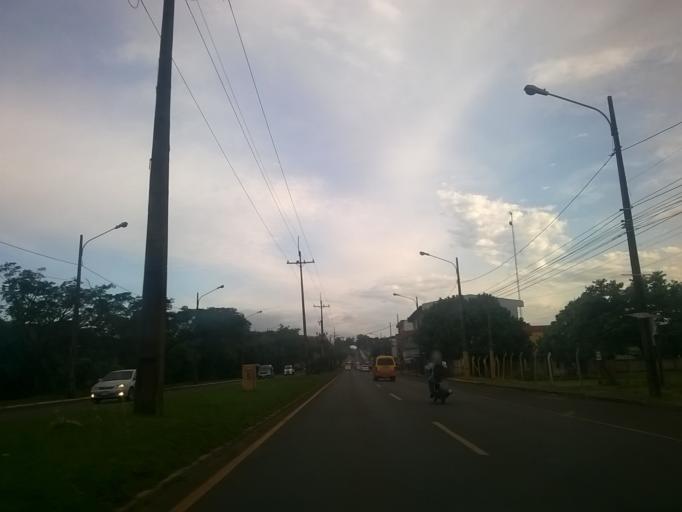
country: PY
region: Alto Parana
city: Presidente Franco
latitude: -25.5303
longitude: -54.6354
